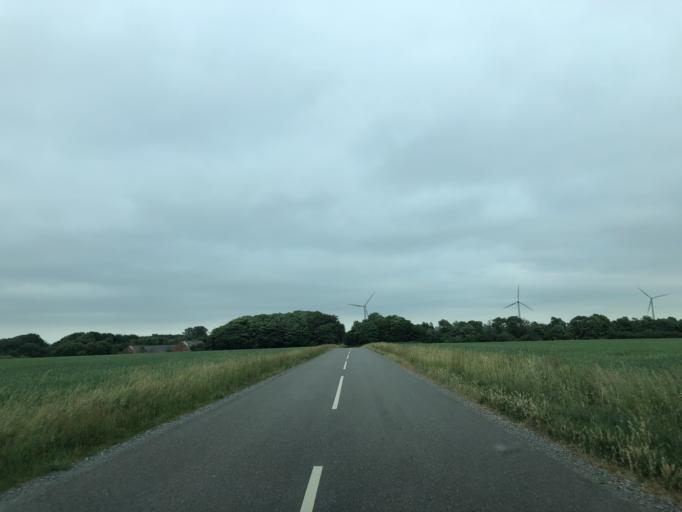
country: DK
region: Central Jutland
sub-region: Holstebro Kommune
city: Holstebro
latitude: 56.2403
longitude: 8.6145
